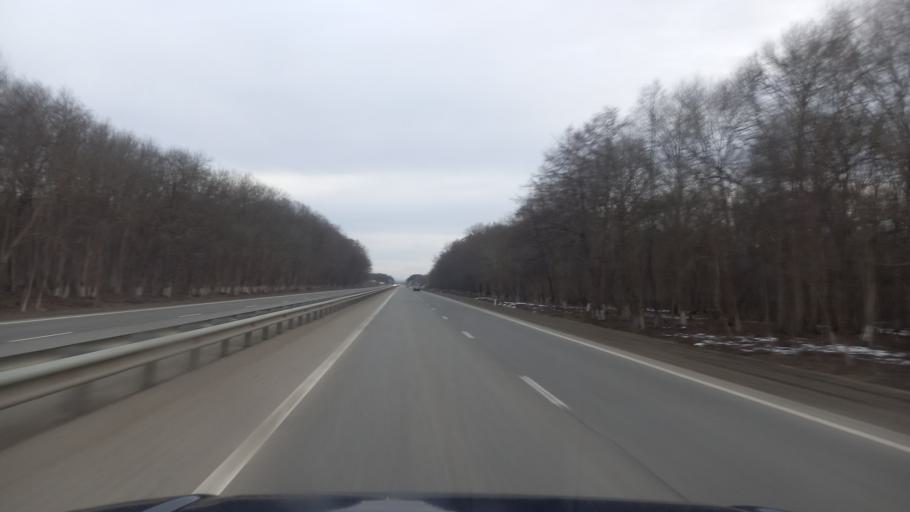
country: RU
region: Adygeya
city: Khanskaya
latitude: 44.7312
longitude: 39.9446
